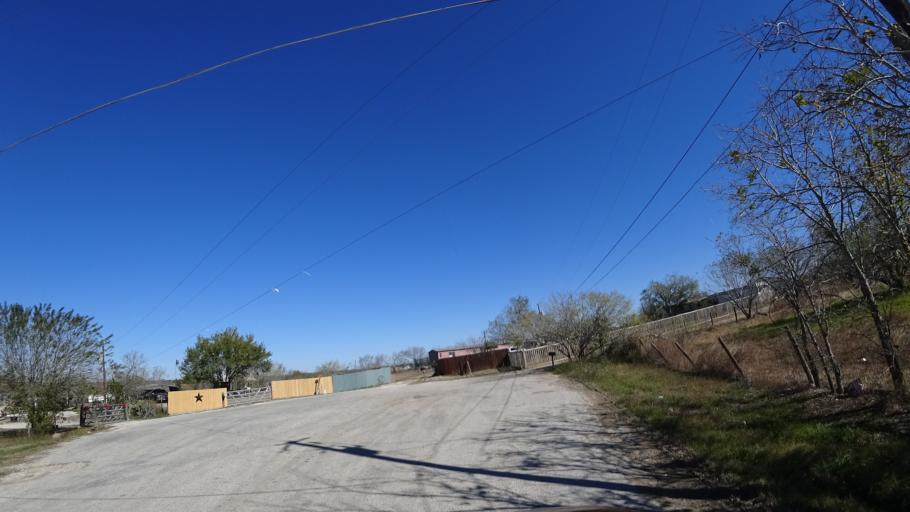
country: US
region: Texas
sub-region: Travis County
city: Garfield
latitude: 30.1113
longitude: -97.5975
